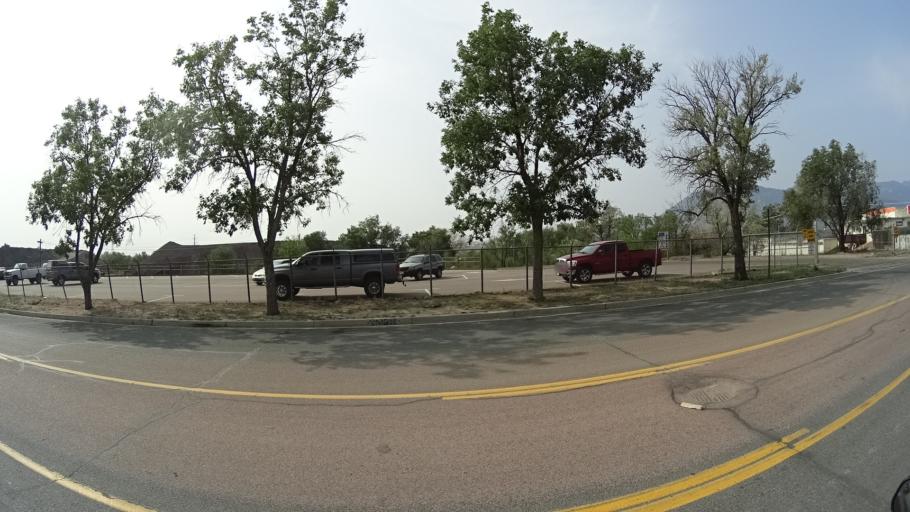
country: US
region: Colorado
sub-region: El Paso County
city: Stratmoor
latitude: 38.7923
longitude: -104.7730
